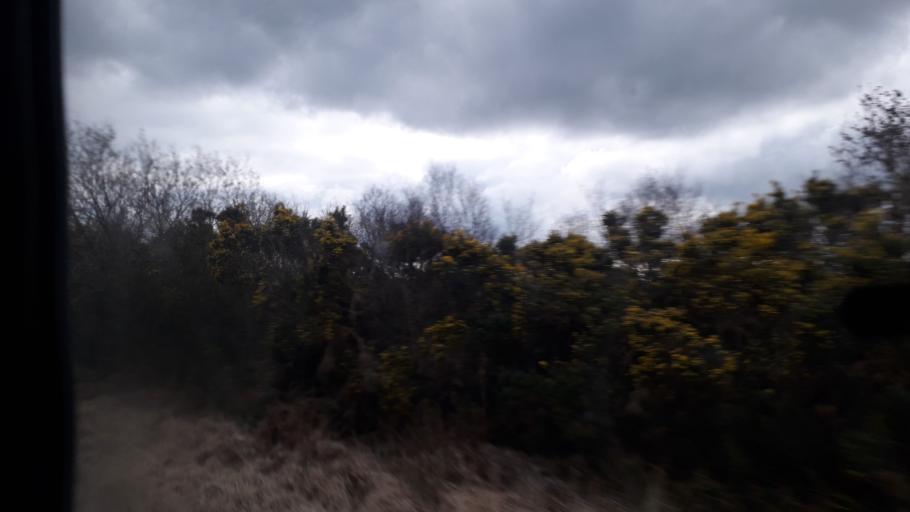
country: IE
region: Leinster
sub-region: An Longfort
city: Longford
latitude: 53.8032
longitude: -7.8578
